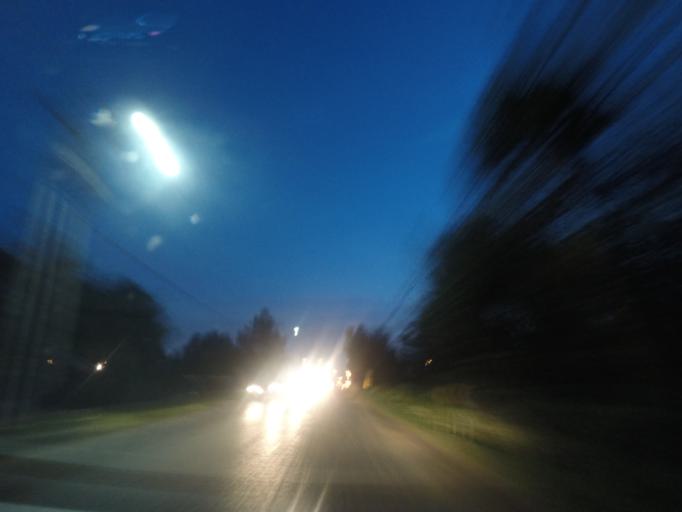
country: BR
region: Parana
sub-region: Pinhais
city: Pinhais
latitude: -25.4937
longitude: -49.1606
